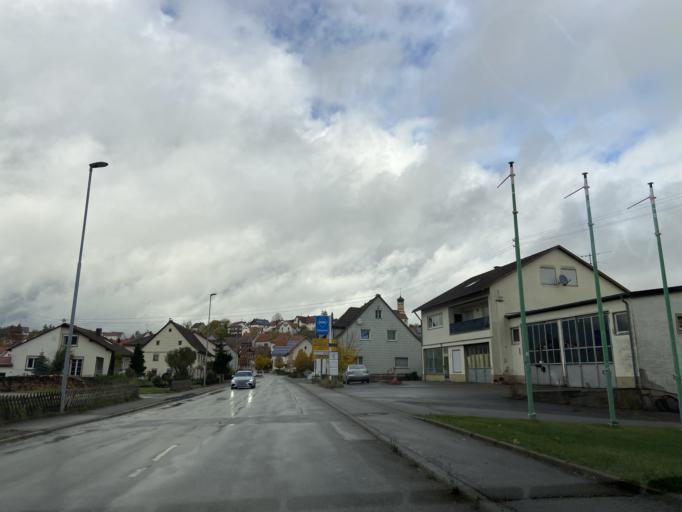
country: DE
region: Baden-Wuerttemberg
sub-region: Tuebingen Region
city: Schwenningen
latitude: 48.1012
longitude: 8.9981
